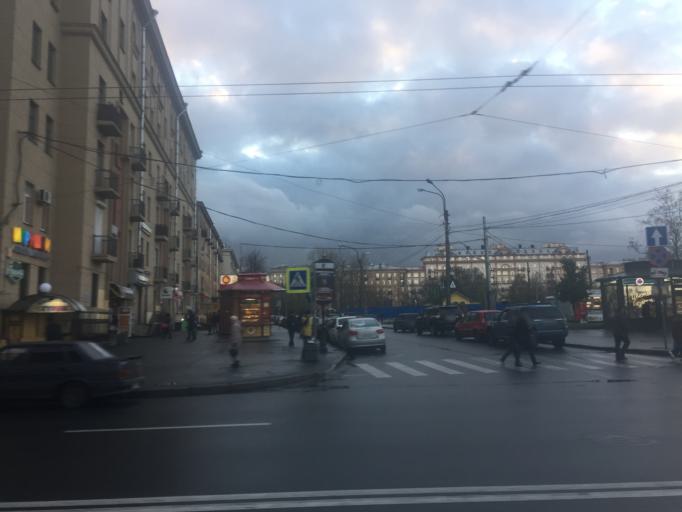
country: RU
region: St.-Petersburg
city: Obukhovo
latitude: 59.8770
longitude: 30.4433
